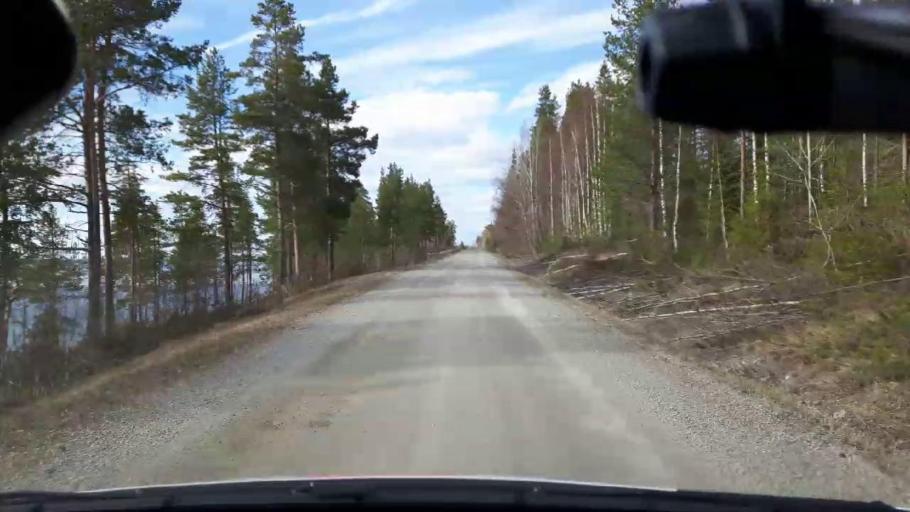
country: SE
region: Jaemtland
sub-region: Bergs Kommun
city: Hoverberg
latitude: 62.7295
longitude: 14.6656
